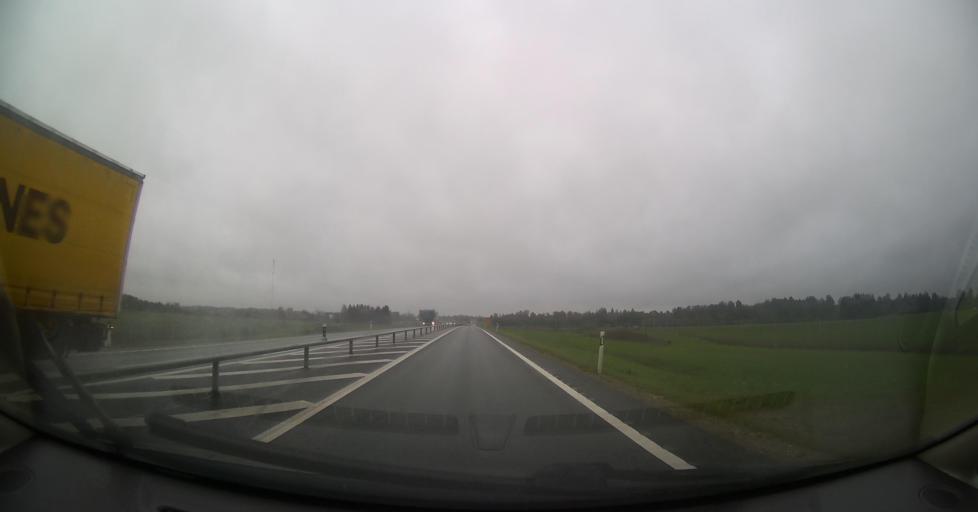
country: EE
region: Jogevamaa
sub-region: Tabivere vald
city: Tabivere
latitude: 58.4393
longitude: 26.4637
